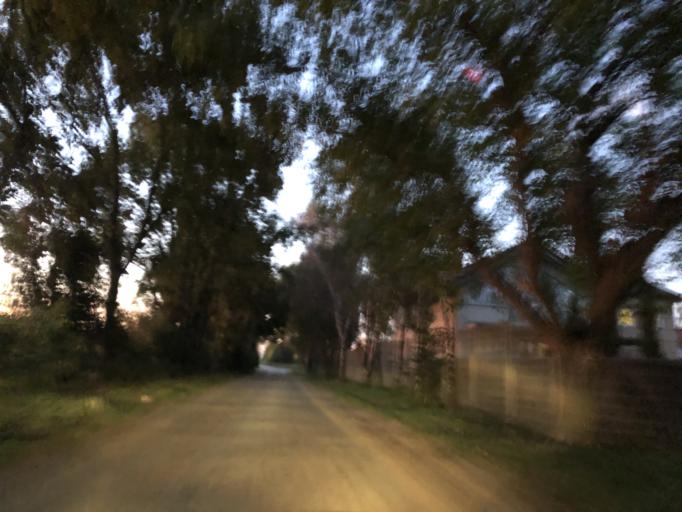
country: DE
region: Hesse
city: Griesheim
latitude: 49.8476
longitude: 8.5496
